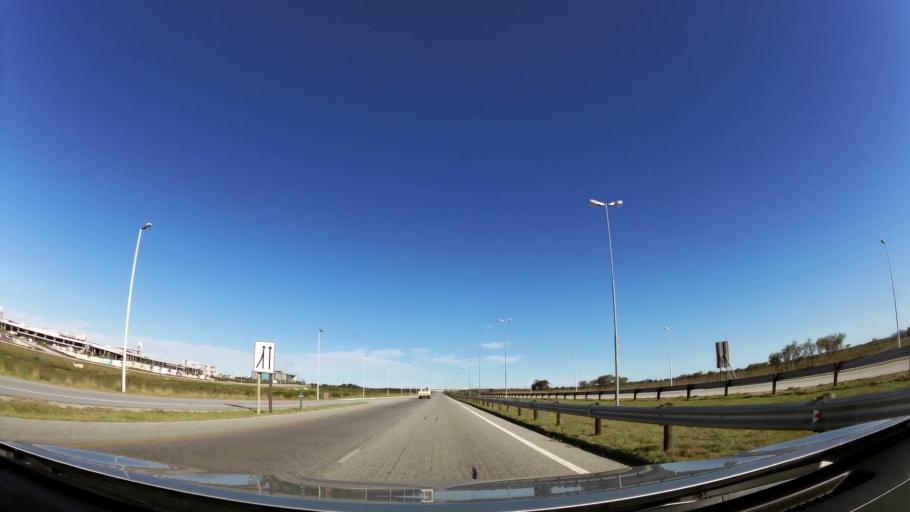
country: ZA
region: Eastern Cape
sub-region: Nelson Mandela Bay Metropolitan Municipality
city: Port Elizabeth
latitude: -33.9473
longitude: 25.4634
